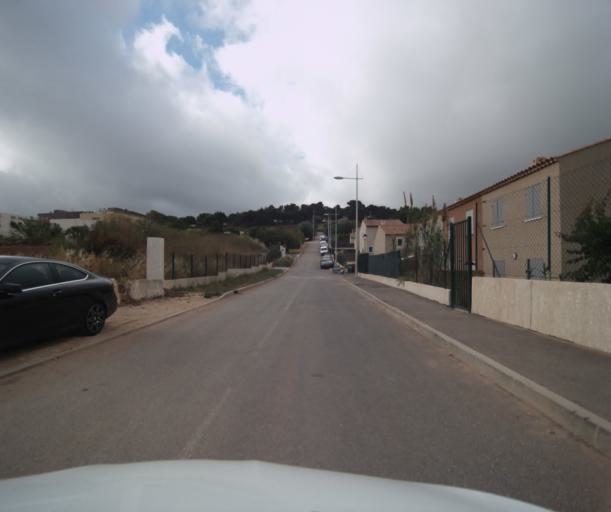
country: FR
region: Provence-Alpes-Cote d'Azur
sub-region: Departement du Var
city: Ollioules
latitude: 43.1271
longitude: 5.8535
